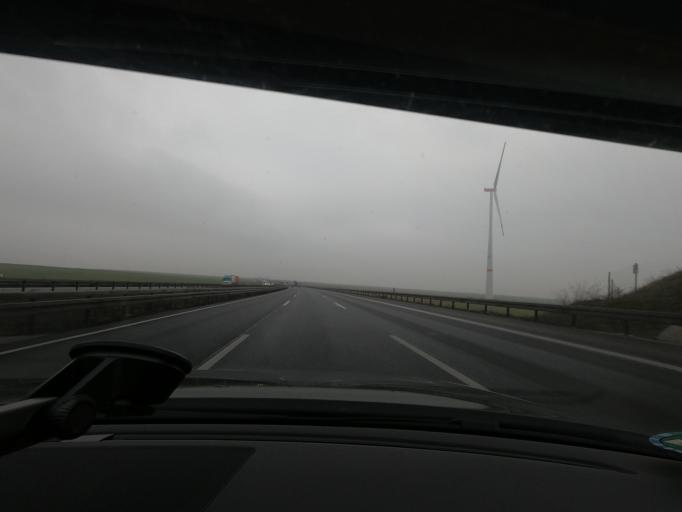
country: DE
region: North Rhine-Westphalia
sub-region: Regierungsbezirk Dusseldorf
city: Juchen
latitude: 51.0572
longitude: 6.4989
